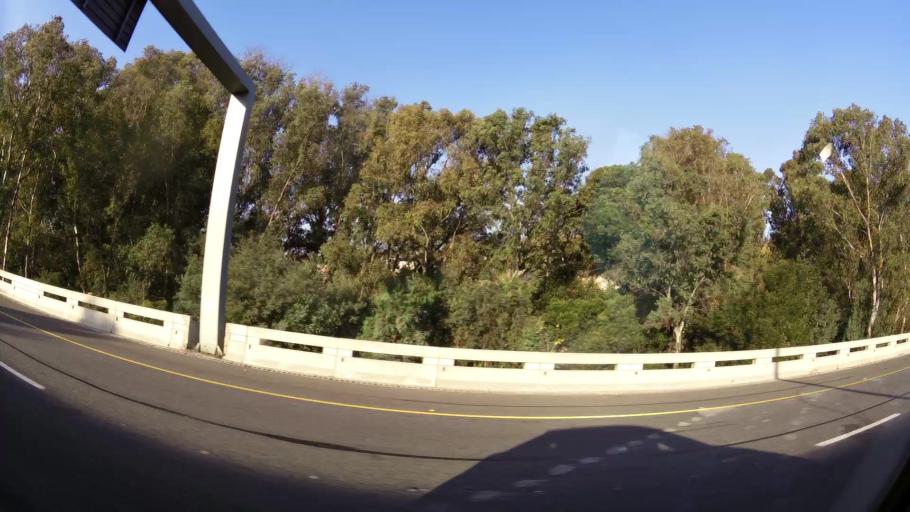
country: ZA
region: Gauteng
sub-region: Ekurhuleni Metropolitan Municipality
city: Germiston
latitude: -26.2478
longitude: 28.1233
